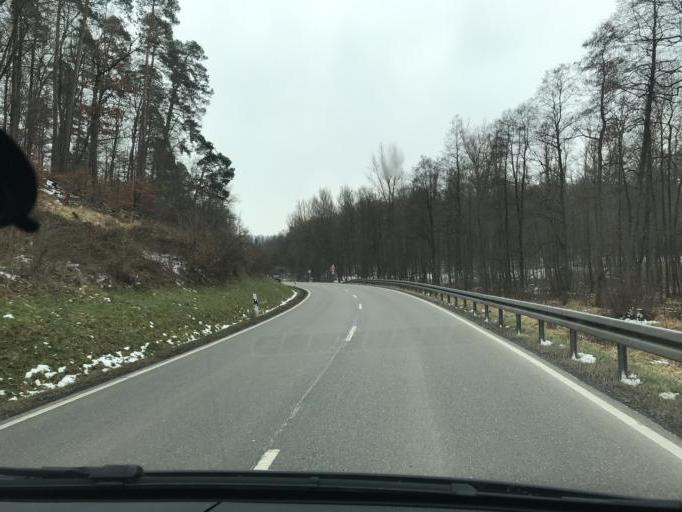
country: DE
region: Baden-Wuerttemberg
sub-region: Regierungsbezirk Stuttgart
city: Sindelfingen
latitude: 48.7162
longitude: 9.0569
